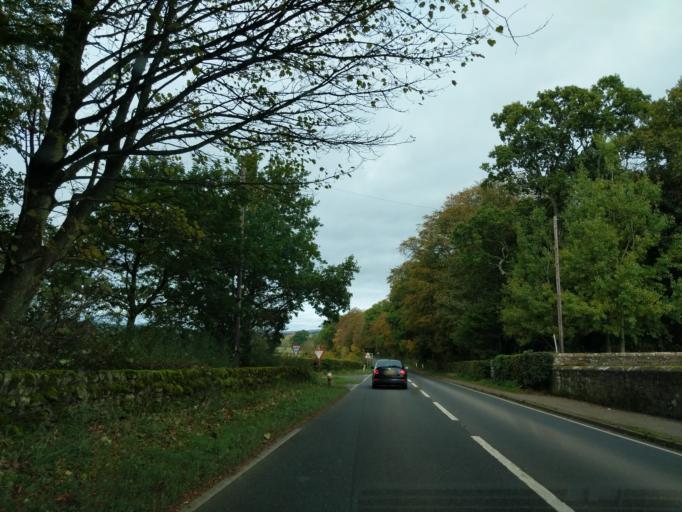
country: GB
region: Scotland
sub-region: Dumfries and Galloway
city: Thornhill
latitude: 55.2501
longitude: -3.7725
